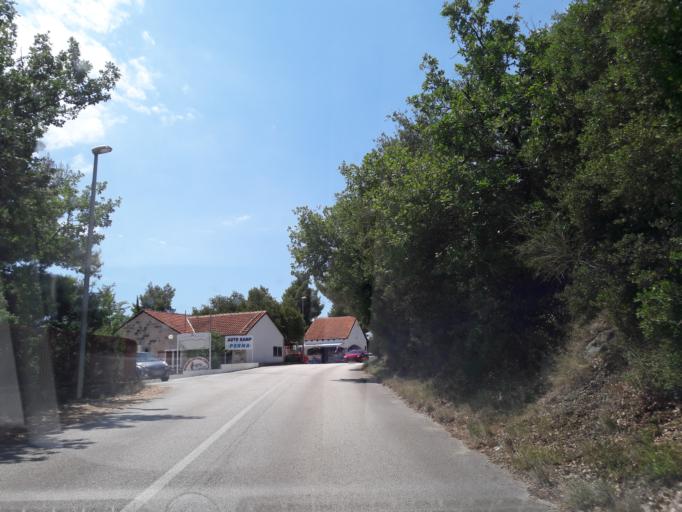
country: HR
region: Dubrovacko-Neretvanska
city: Korcula
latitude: 42.9767
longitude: 17.1336
